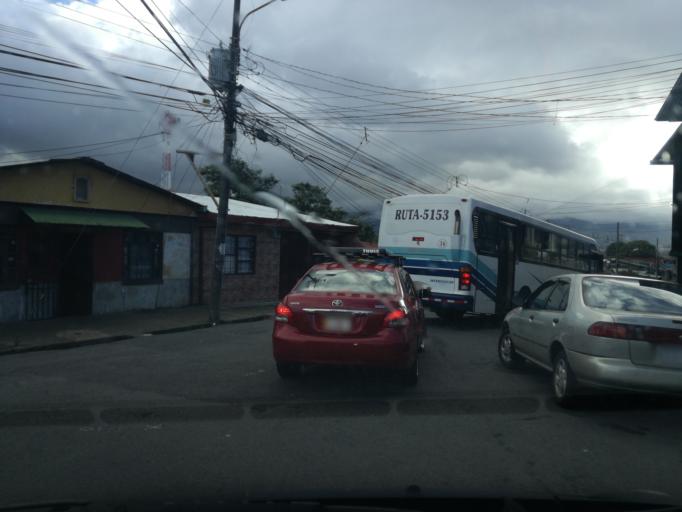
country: CR
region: San Jose
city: San Pedro
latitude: 9.9251
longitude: -84.0477
